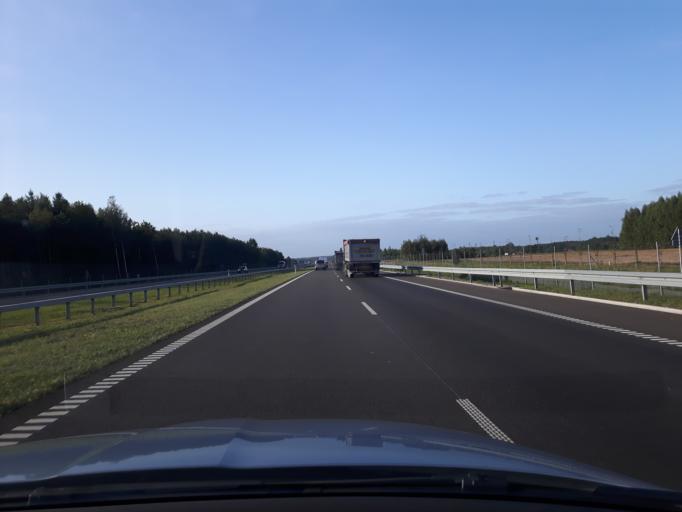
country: PL
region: Masovian Voivodeship
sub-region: Powiat radomski
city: Wolanow
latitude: 51.3780
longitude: 21.0188
